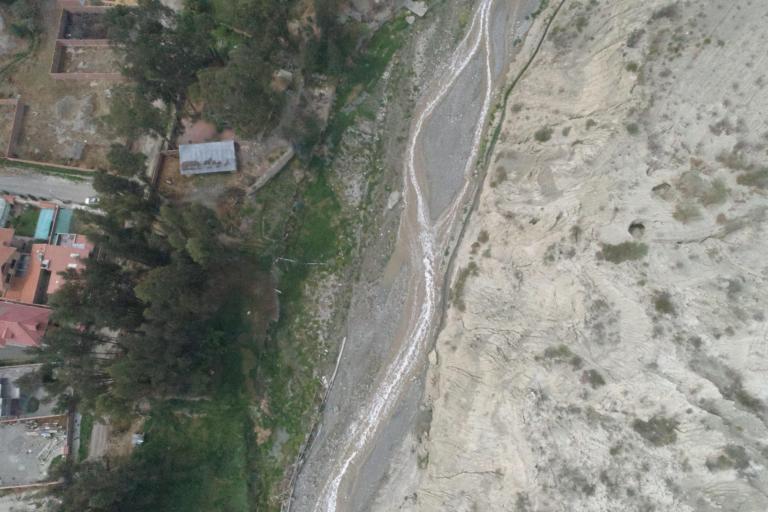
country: BO
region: La Paz
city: La Paz
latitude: -16.6018
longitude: -68.0663
